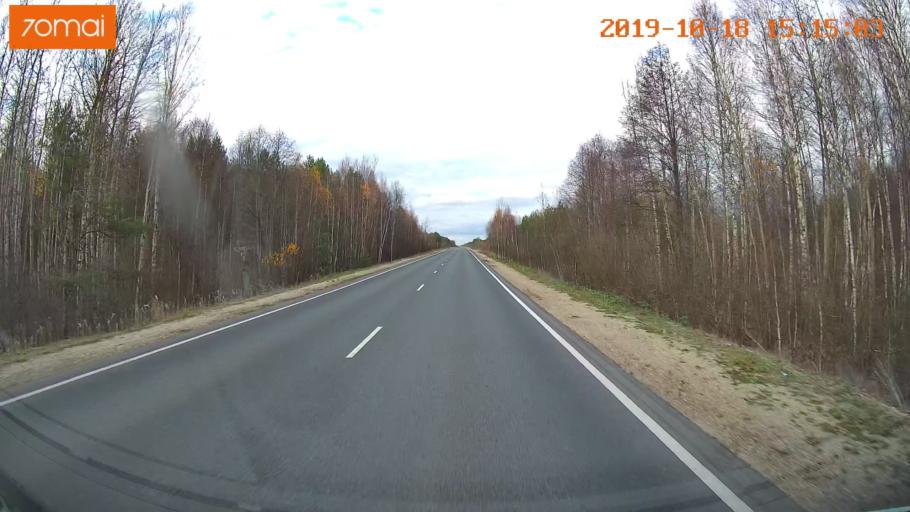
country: RU
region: Vladimir
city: Gus'-Khrustal'nyy
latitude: 55.6127
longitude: 40.7216
